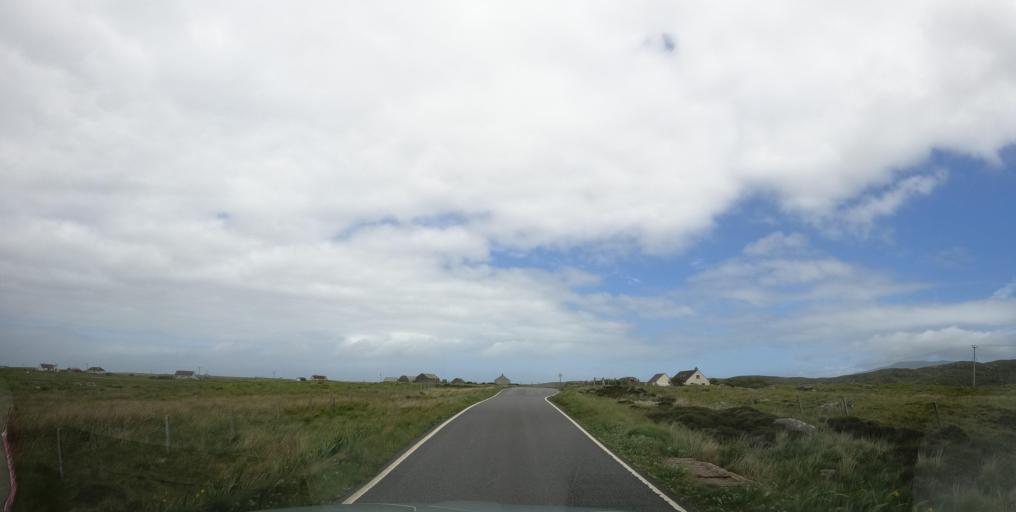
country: GB
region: Scotland
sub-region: Eilean Siar
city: Isle of South Uist
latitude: 57.2083
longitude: -7.3935
